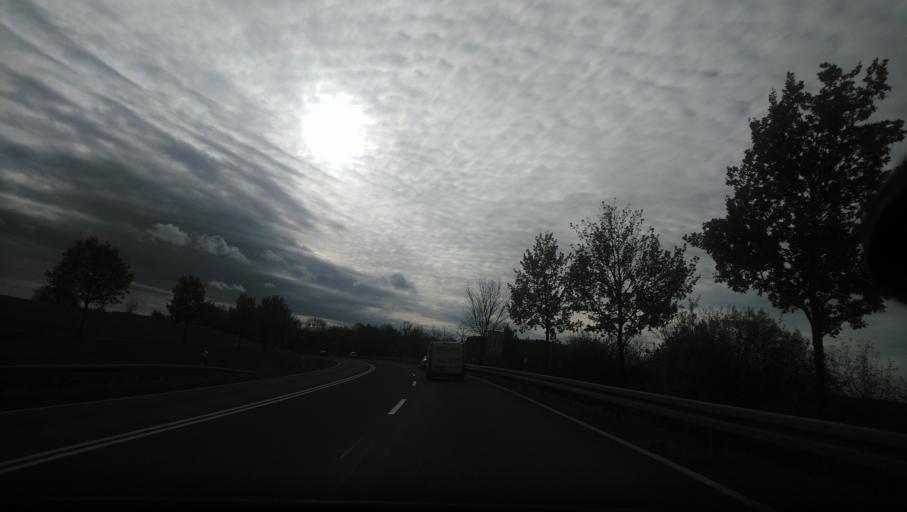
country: DE
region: Saxony
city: Zwonitz
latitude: 50.6342
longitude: 12.8196
